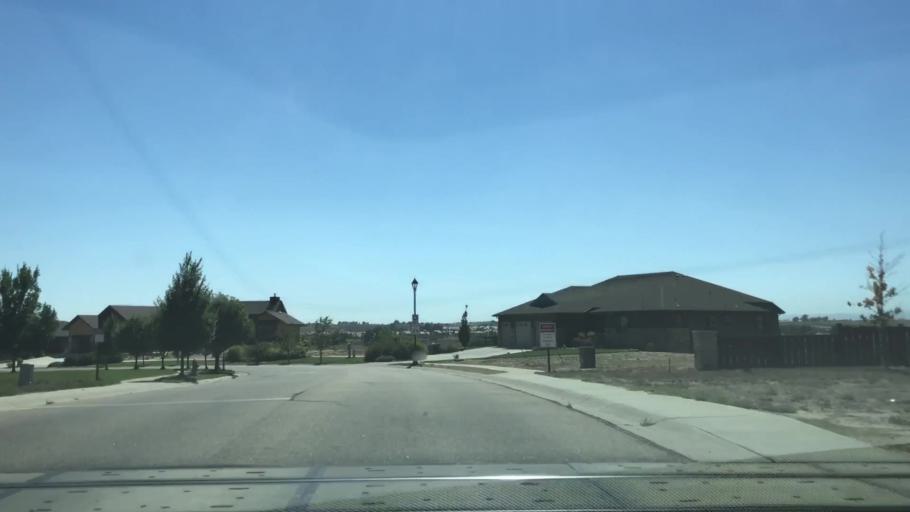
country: US
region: Colorado
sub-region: Larimer County
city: Loveland
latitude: 40.4000
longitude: -104.9821
